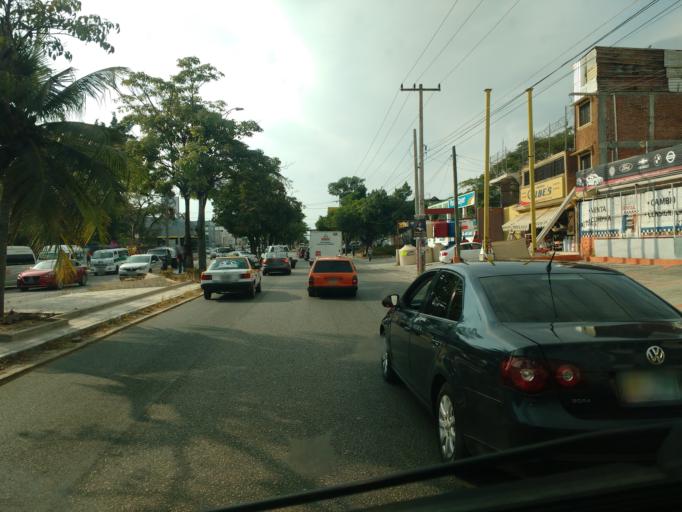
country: MX
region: Chiapas
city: Tuxtla Gutierrez
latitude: 16.7483
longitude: -93.0877
